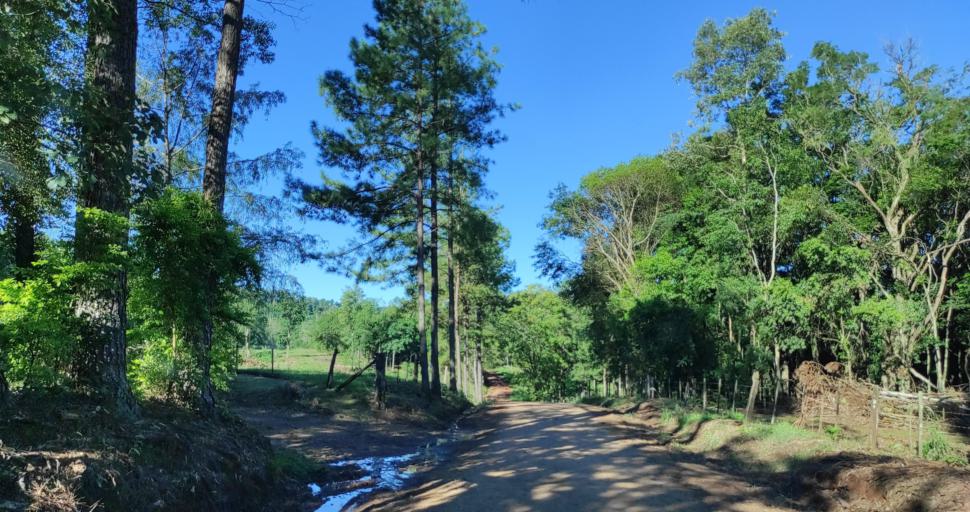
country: AR
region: Misiones
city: Capiovi
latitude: -26.9074
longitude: -54.9986
